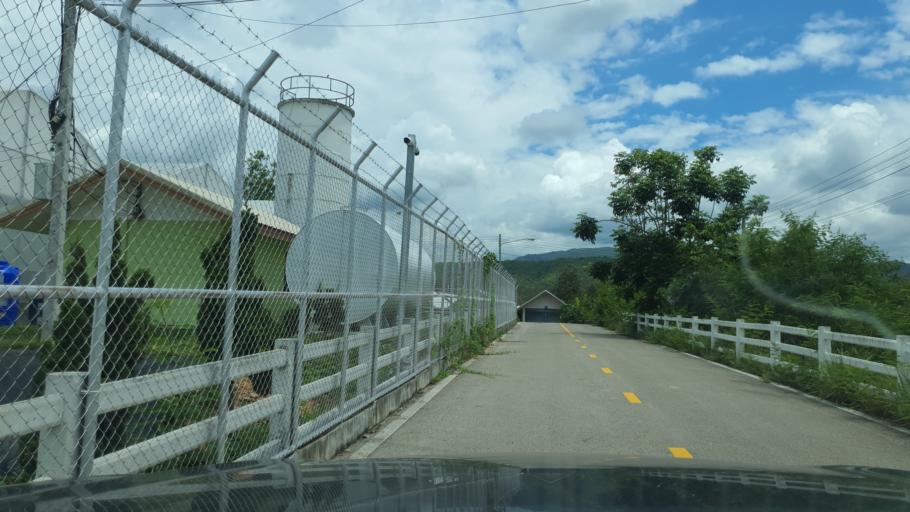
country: TH
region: Chiang Mai
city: San Sai
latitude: 18.9255
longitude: 99.0558
